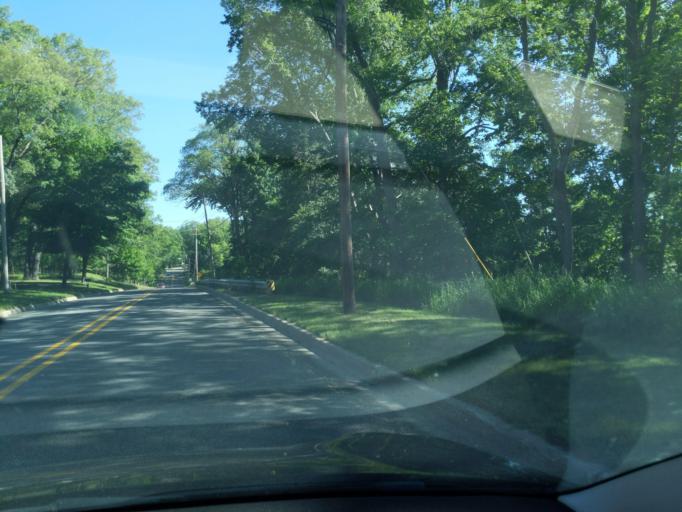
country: US
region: Michigan
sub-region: Muskegon County
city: Montague
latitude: 43.4077
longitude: -86.3601
